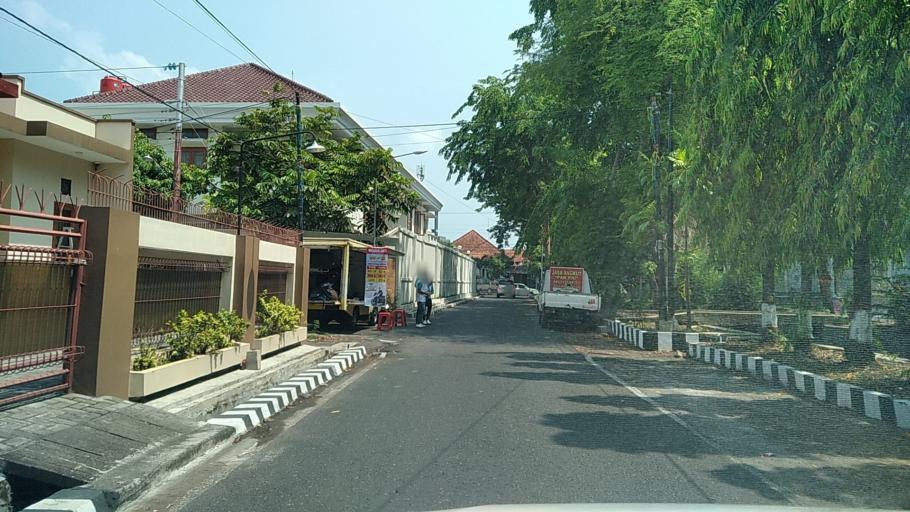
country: ID
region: Central Java
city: Semarang
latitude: -7.0073
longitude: 110.4392
